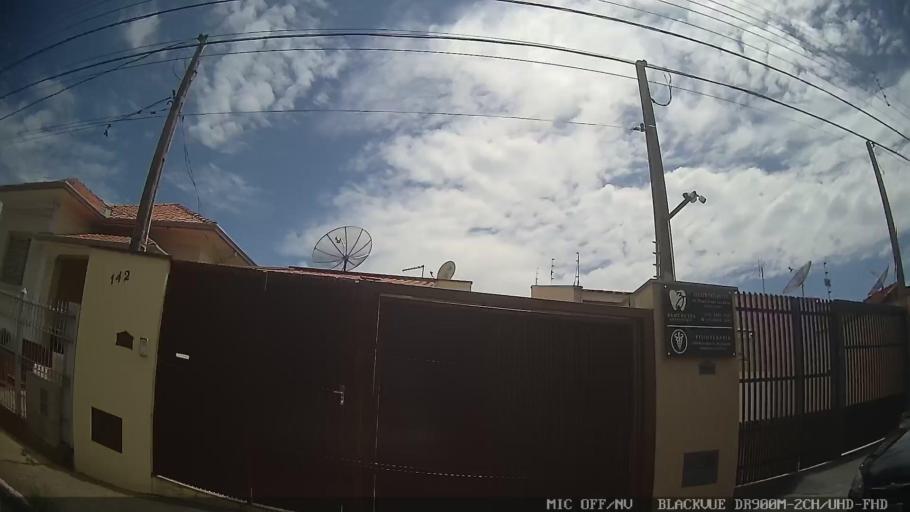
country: BR
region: Sao Paulo
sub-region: Laranjal Paulista
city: Laranjal Paulista
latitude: -23.0417
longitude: -47.8355
